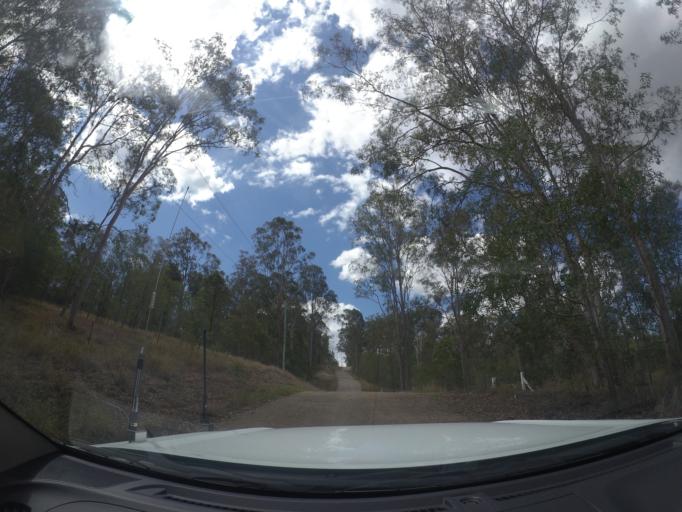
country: AU
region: Queensland
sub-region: Logan
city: Cedar Vale
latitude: -27.8995
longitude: 153.0007
